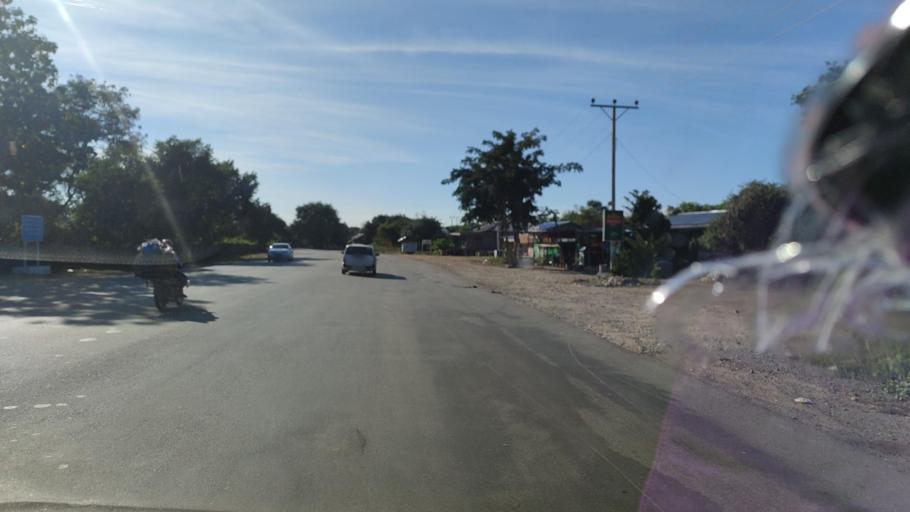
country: MM
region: Mandalay
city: Yamethin
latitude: 20.7516
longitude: 96.2704
